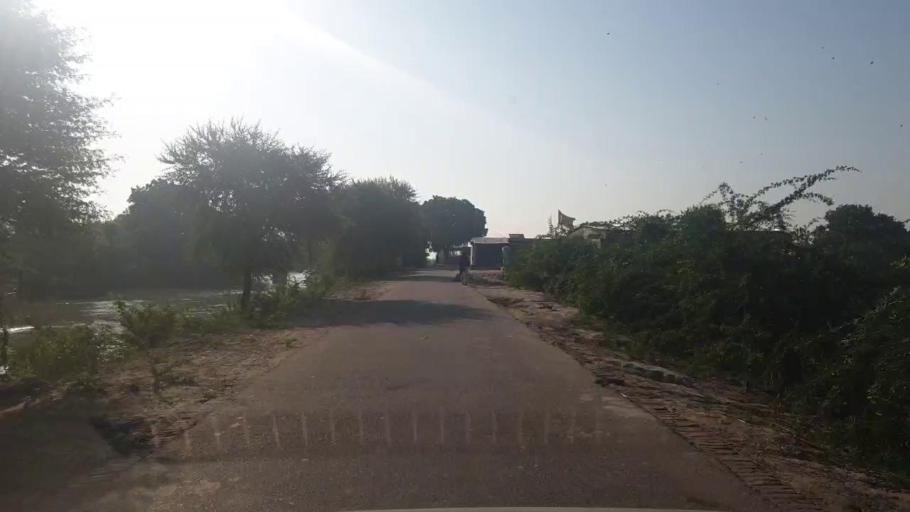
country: PK
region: Sindh
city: Tando Bago
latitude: 24.7211
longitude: 68.9403
